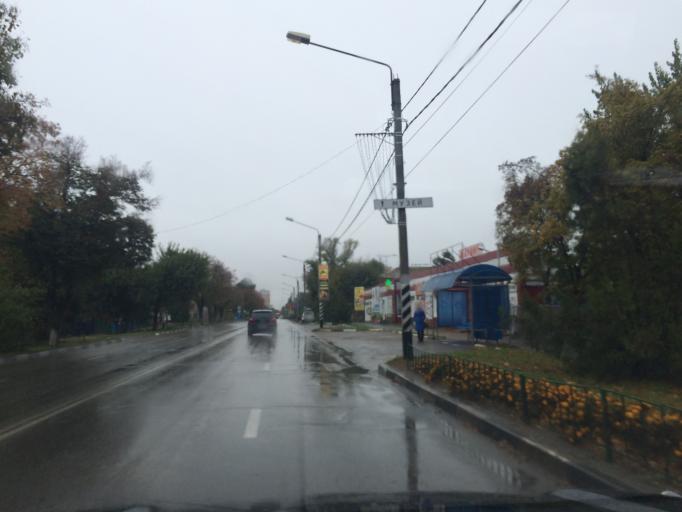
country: RU
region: Rostov
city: Azov
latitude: 47.1000
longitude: 39.4404
